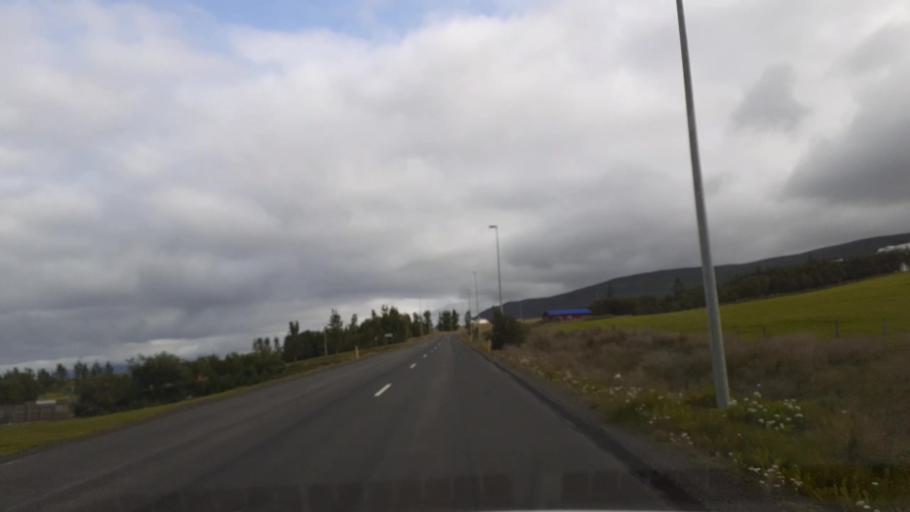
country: IS
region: Northeast
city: Akureyri
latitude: 65.7473
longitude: -18.0804
